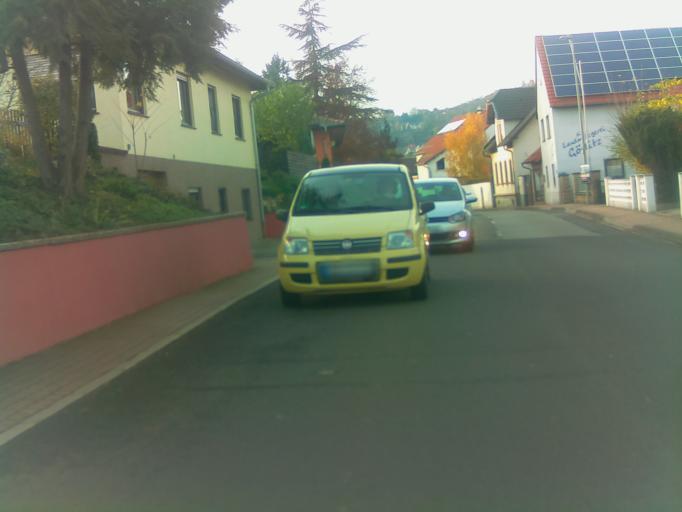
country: DE
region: Rheinland-Pfalz
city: Kleinkarlbach
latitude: 49.5399
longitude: 8.1586
